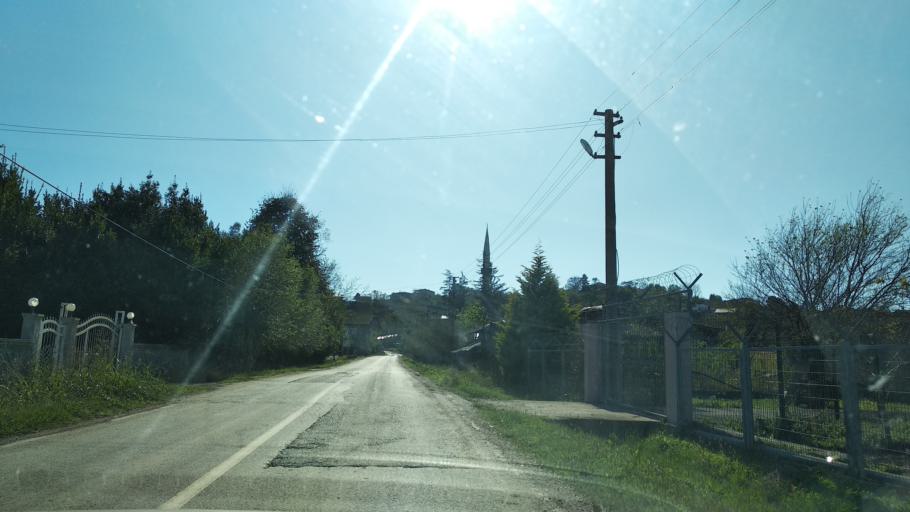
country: TR
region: Sakarya
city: Ortakoy
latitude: 41.0367
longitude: 30.5974
